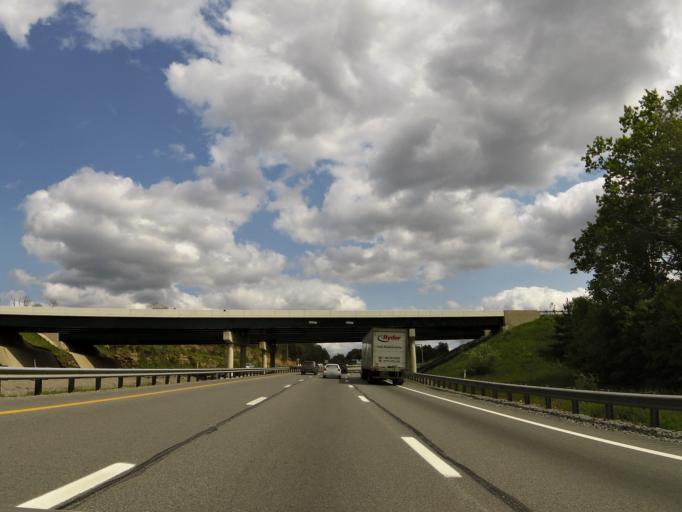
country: US
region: West Virginia
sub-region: Raleigh County
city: Prosperity
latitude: 37.8360
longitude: -81.2163
